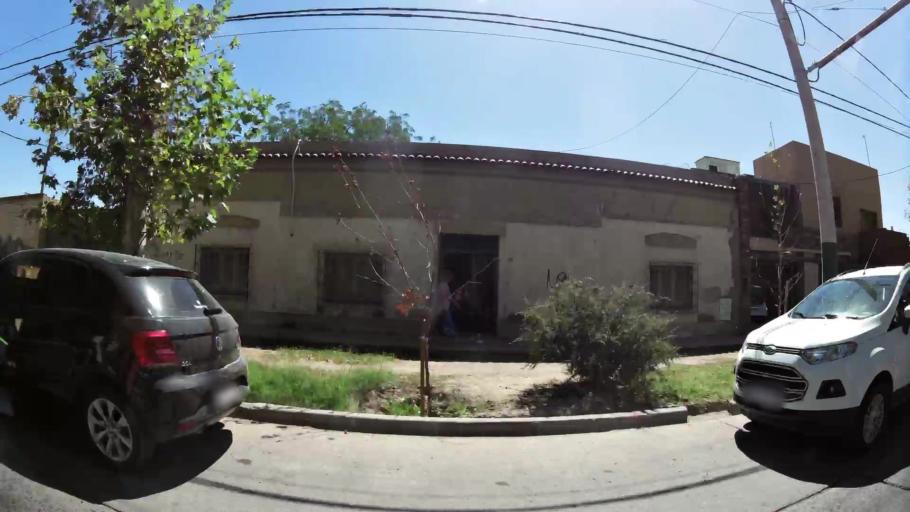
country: AR
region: Mendoza
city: Mendoza
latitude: -32.8945
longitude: -68.8193
